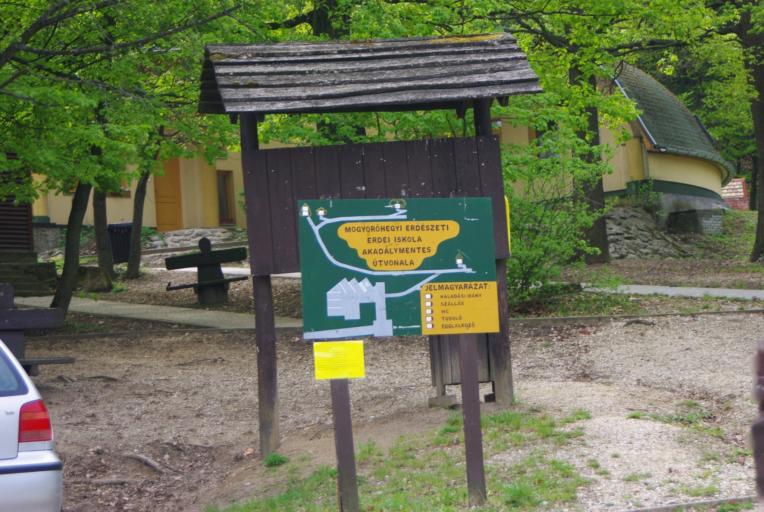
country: HU
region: Pest
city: Visegrad
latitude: 47.7979
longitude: 18.9934
